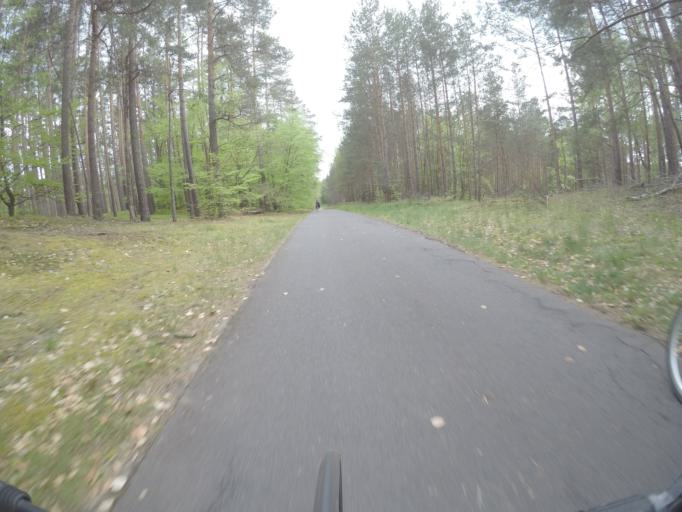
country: DE
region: Brandenburg
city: Biesenthal
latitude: 52.8093
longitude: 13.6328
